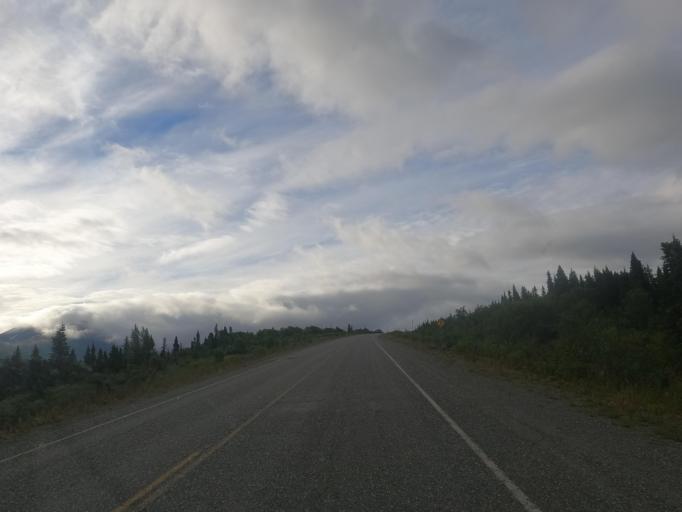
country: CA
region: Yukon
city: Haines Junction
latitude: 59.9466
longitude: -136.8024
